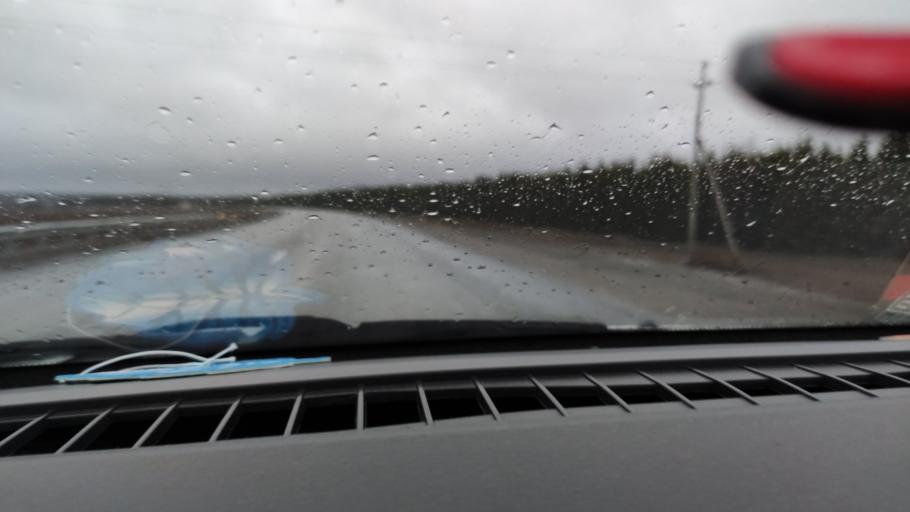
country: RU
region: Udmurtiya
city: Alnashi
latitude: 56.0816
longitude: 52.4049
